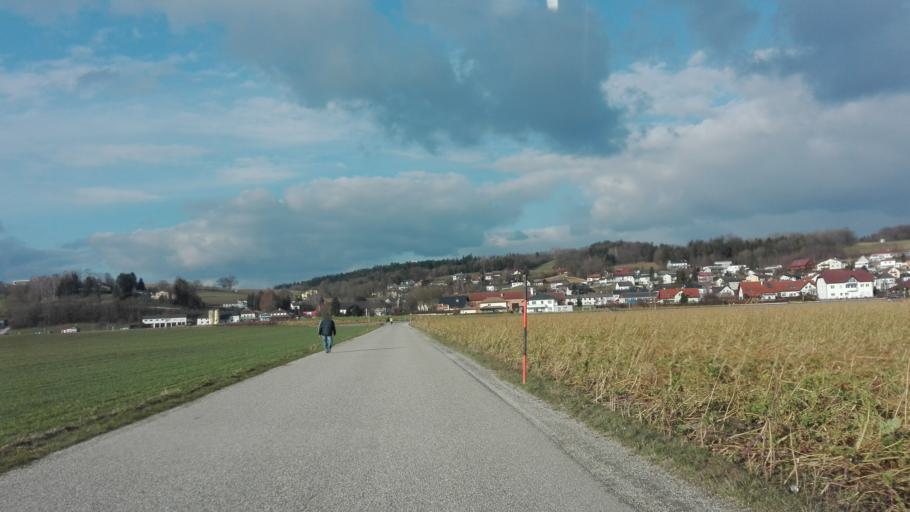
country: AT
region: Upper Austria
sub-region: Politischer Bezirk Perg
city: Perg
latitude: 48.2470
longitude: 14.6192
